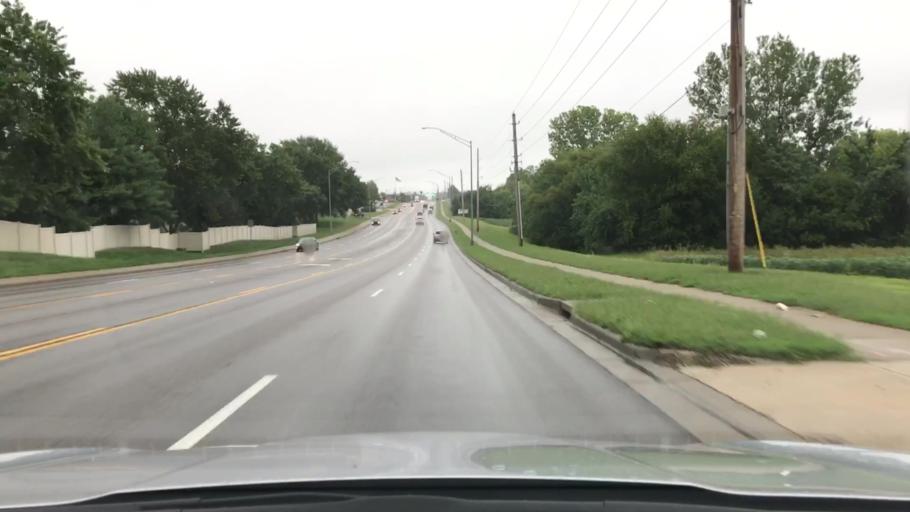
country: US
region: Missouri
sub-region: Cass County
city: Raymore
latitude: 38.8122
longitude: -94.4824
